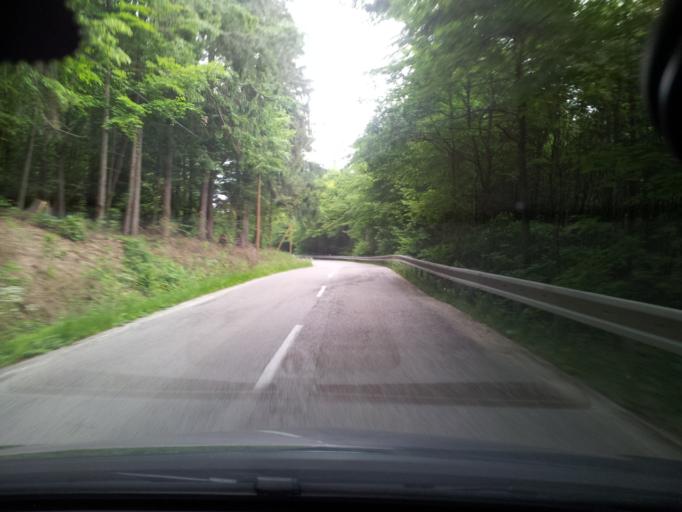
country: SK
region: Nitriansky
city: Partizanske
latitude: 48.5910
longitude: 18.4533
